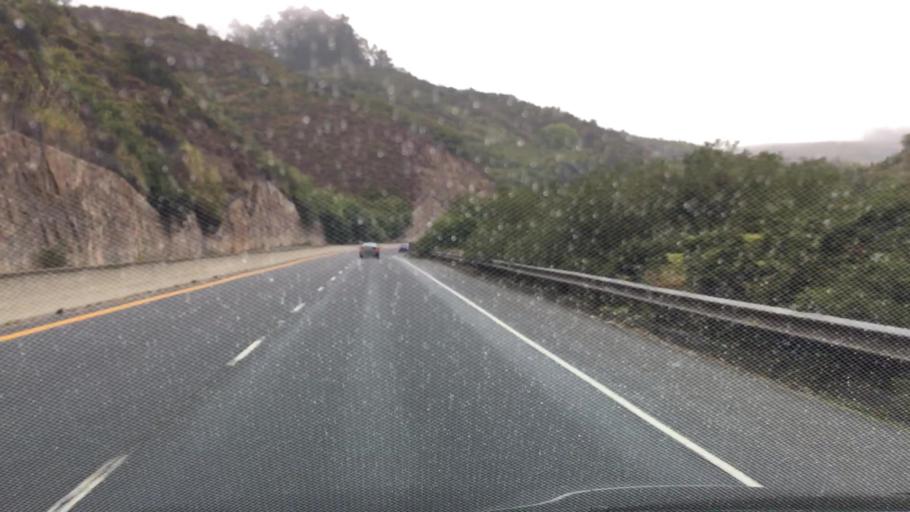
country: US
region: California
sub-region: San Mateo County
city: Highlands-Baywood Park
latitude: 37.4931
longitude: -122.3810
